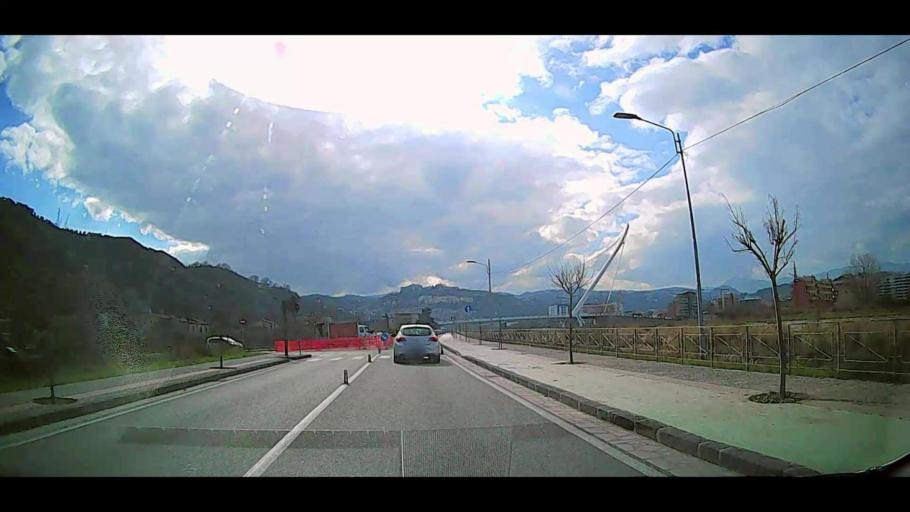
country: IT
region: Calabria
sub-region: Provincia di Cosenza
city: Cosenza
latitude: 39.3021
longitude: 16.2628
